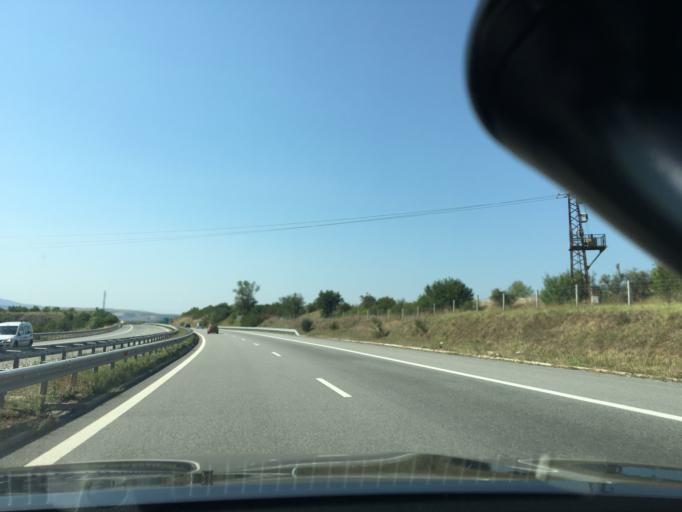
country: BG
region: Kyustendil
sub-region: Obshtina Bobovdol
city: Bobovdol
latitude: 42.3492
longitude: 23.0957
